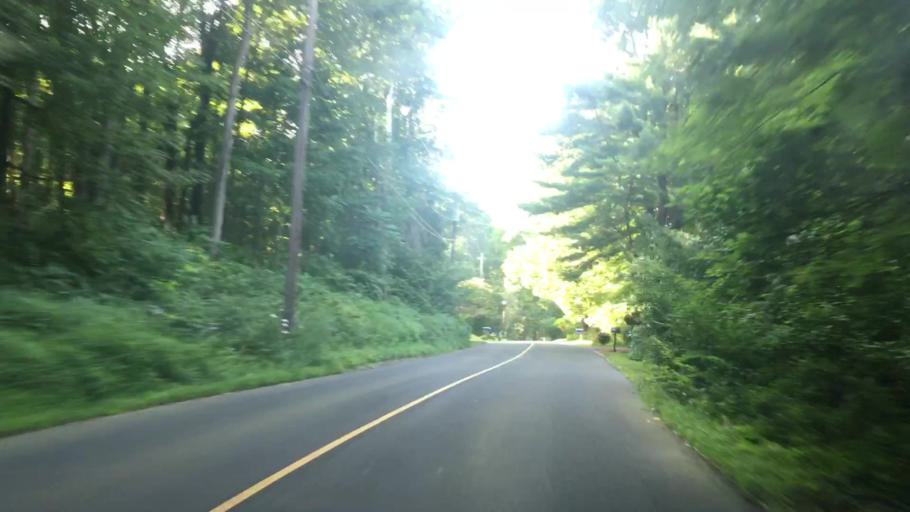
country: US
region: Connecticut
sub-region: Middlesex County
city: Chester Center
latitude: 41.3962
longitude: -72.4538
